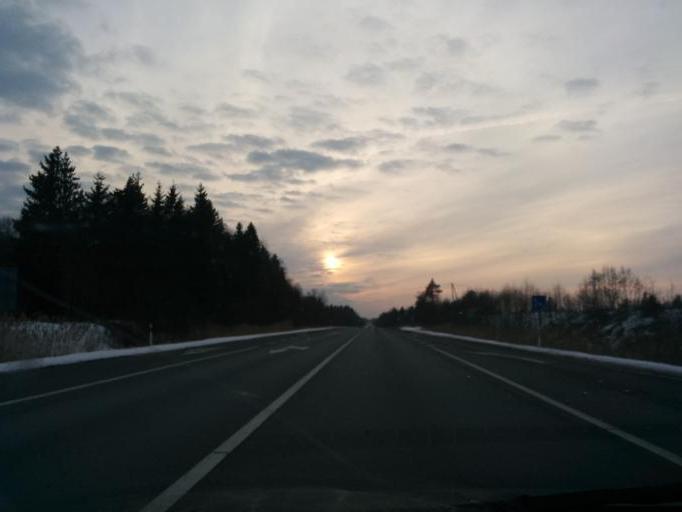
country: LV
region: Raunas
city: Rauna
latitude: 57.3080
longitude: 25.6277
